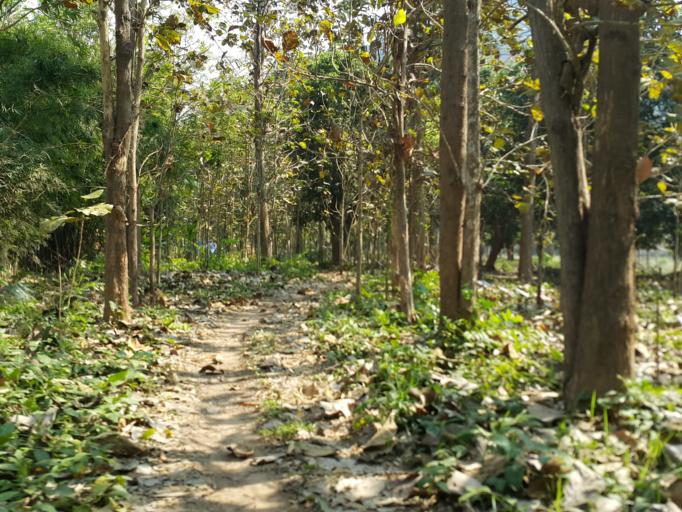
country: TH
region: Sukhothai
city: Thung Saliam
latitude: 17.3241
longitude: 99.5040
